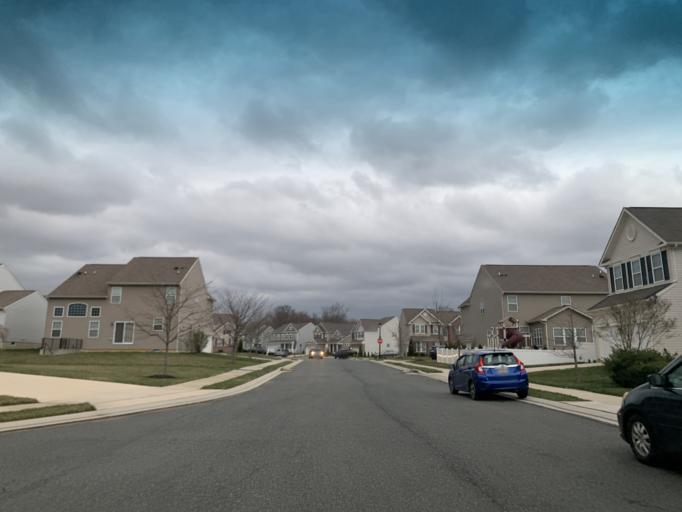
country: US
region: Maryland
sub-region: Harford County
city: Perryman
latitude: 39.4948
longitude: -76.2067
